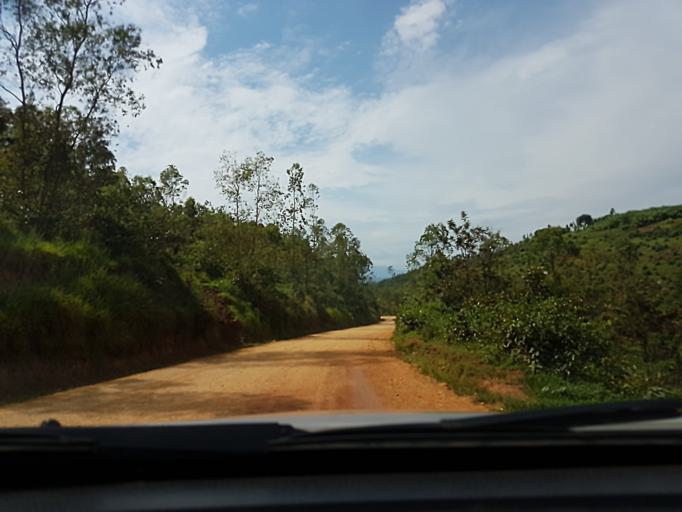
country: CD
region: South Kivu
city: Bukavu
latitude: -2.6322
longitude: 28.8758
